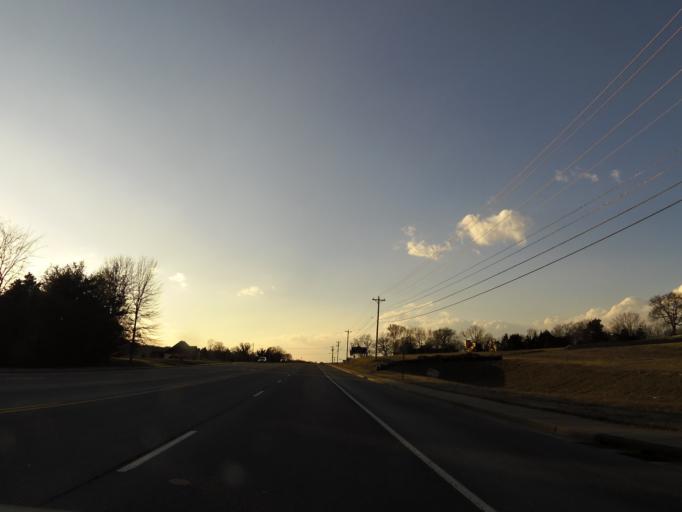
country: US
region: Tennessee
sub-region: Wilson County
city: Lebanon
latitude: 36.2304
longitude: -86.3792
